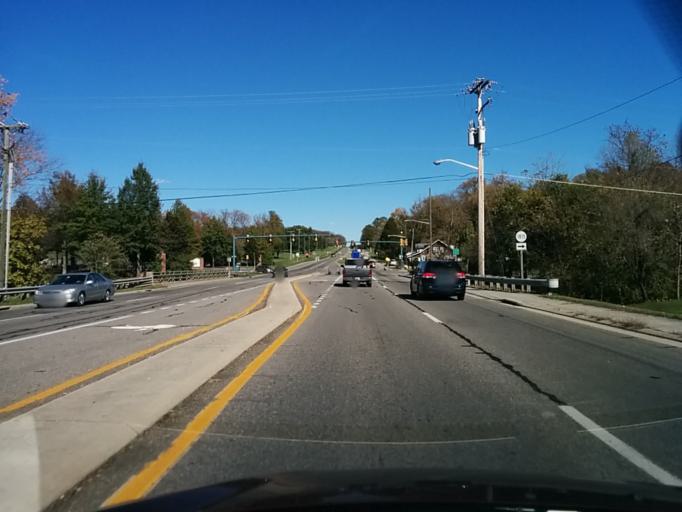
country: US
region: Virginia
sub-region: Roanoke County
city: Hollins
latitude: 37.3510
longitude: -79.9425
